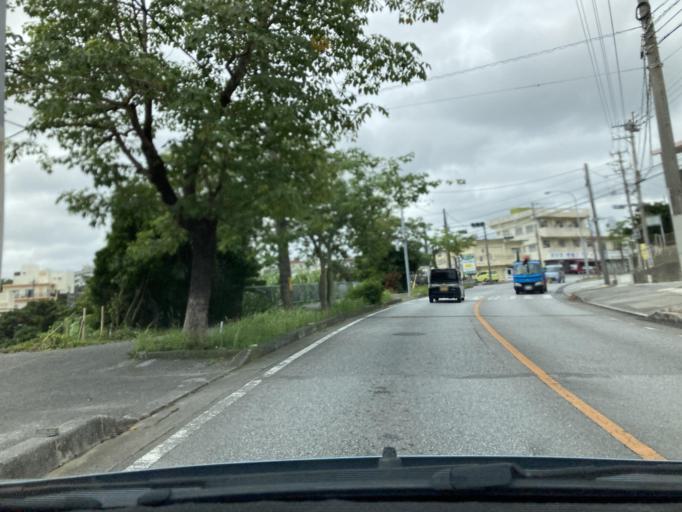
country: JP
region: Okinawa
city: Ginowan
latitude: 26.2362
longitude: 127.7518
